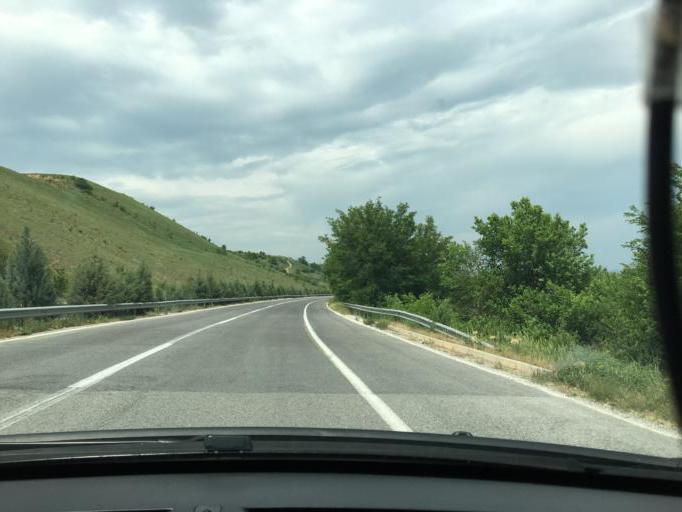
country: MK
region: Demir Kapija
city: Demir Kapija
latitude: 41.4184
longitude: 22.1954
